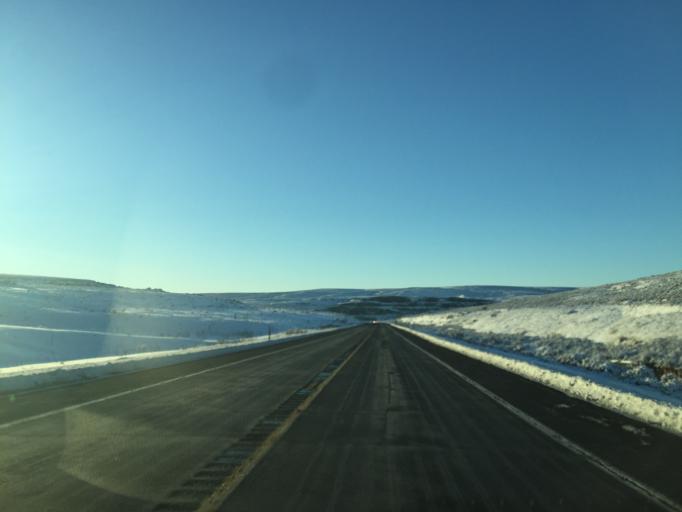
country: US
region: Washington
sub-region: Grant County
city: Soap Lake
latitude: 47.6069
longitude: -119.6504
